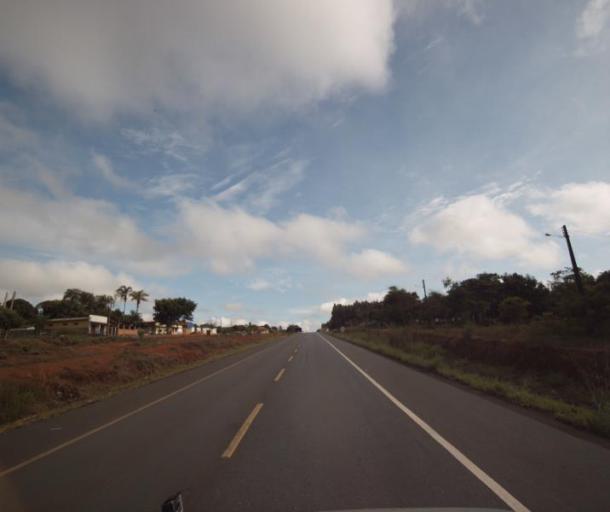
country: BR
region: Goias
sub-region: Barro Alto
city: Barro Alto
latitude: -15.2128
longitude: -48.6987
